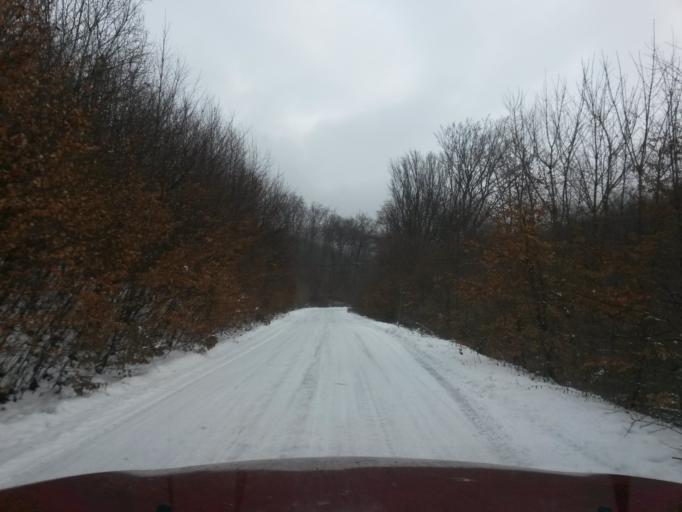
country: SK
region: Kosicky
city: Secovce
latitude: 48.8044
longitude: 21.5094
